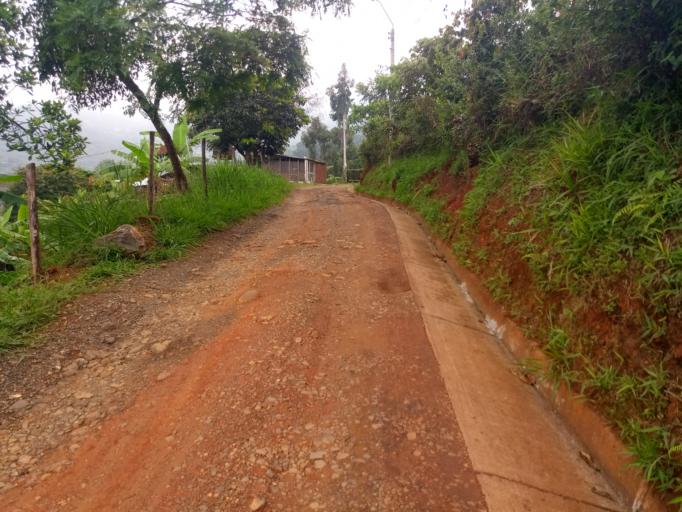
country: CO
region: Valle del Cauca
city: Cali
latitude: 3.5074
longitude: -76.5640
